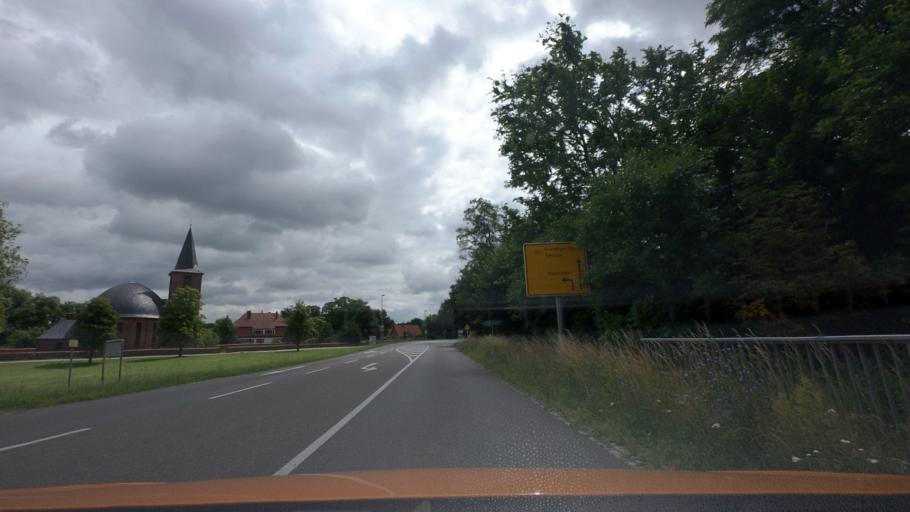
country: DE
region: Brandenburg
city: Bliesdorf
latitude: 52.6771
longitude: 14.1565
